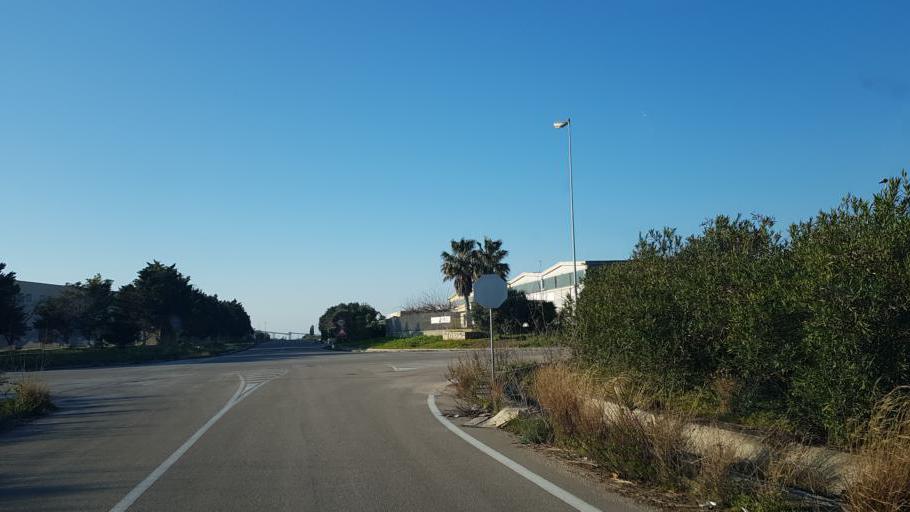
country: IT
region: Apulia
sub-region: Provincia di Brindisi
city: La Rosa
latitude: 40.6252
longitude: 17.9702
